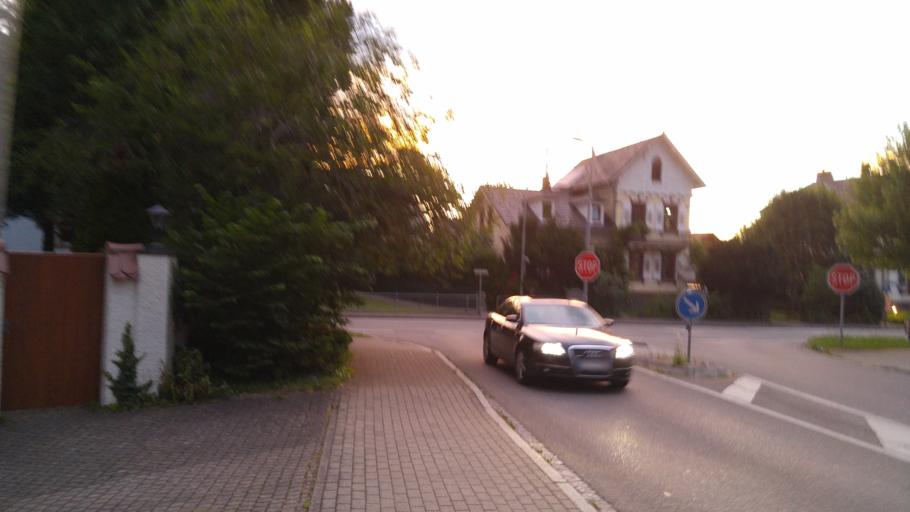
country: DE
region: Baden-Wuerttemberg
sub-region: Freiburg Region
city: Sulzburg
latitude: 47.8789
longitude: 7.7305
